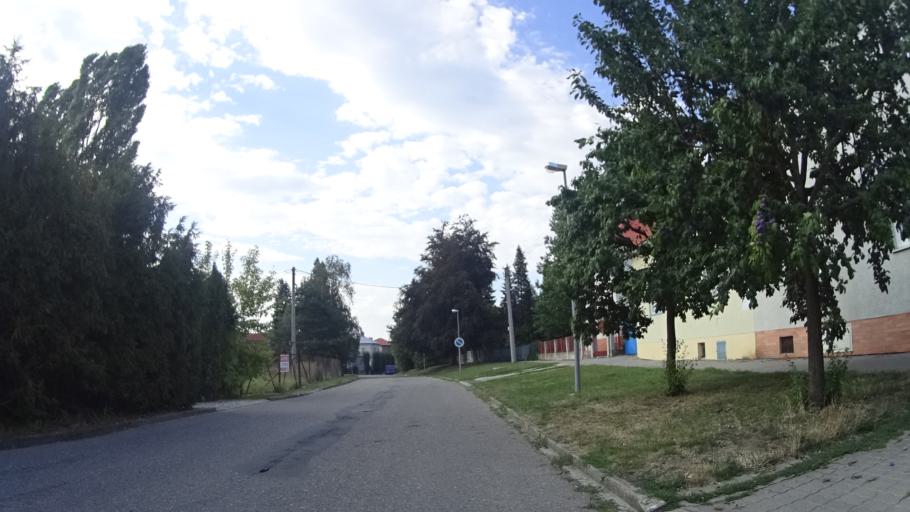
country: CZ
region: Zlin
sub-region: Okres Zlin
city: Napajedla
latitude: 49.1632
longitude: 17.5144
